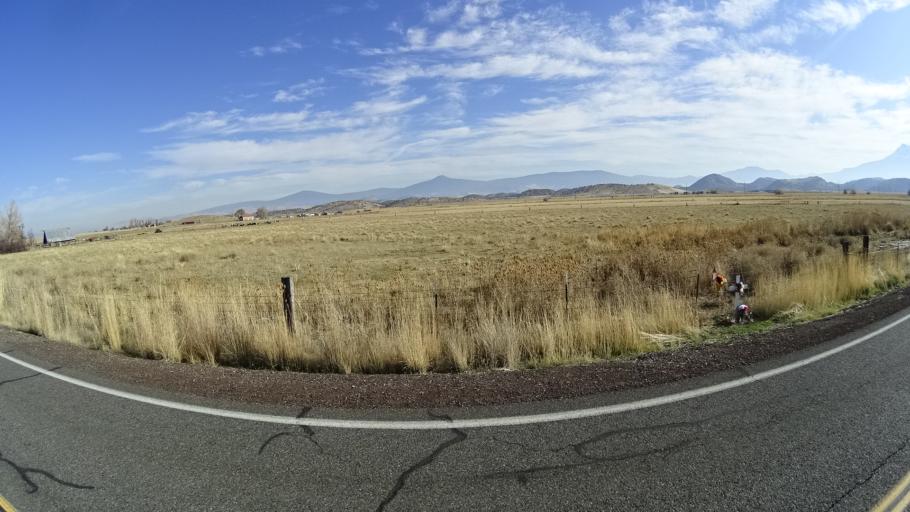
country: US
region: California
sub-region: Siskiyou County
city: Montague
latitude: 41.6087
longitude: -122.5297
